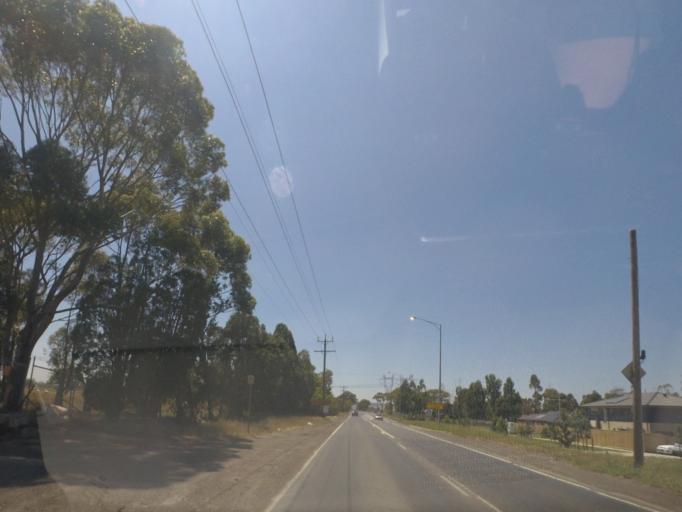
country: AU
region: Victoria
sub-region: Whittlesea
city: Epping
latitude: -37.6065
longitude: 145.0117
